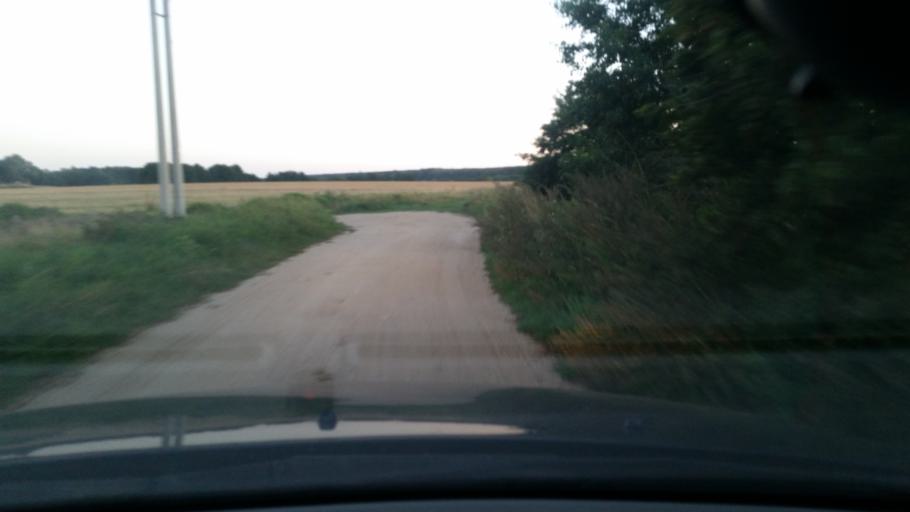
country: PL
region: Pomeranian Voivodeship
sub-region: Powiat wejherowski
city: Choczewo
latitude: 54.7766
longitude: 17.7914
